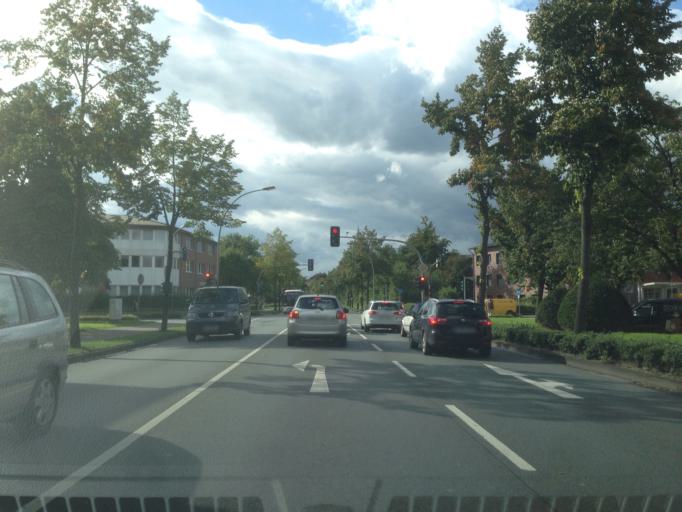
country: DE
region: North Rhine-Westphalia
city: Ludinghausen
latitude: 51.7678
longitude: 7.4449
